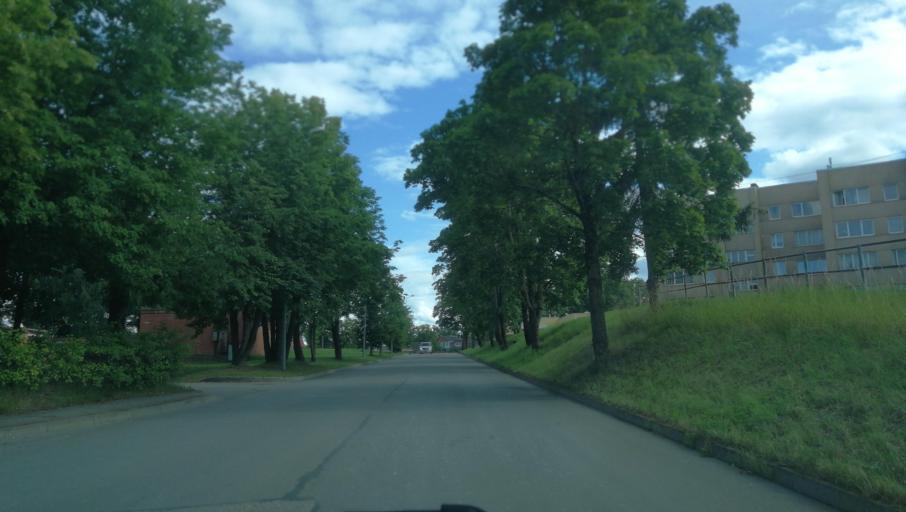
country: LV
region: Cesu Rajons
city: Cesis
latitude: 57.3213
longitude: 25.2883
